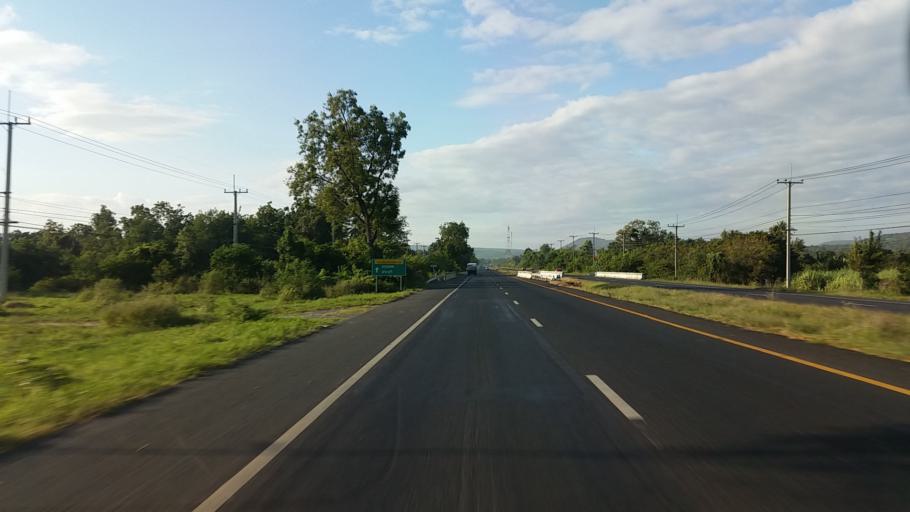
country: TH
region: Lop Buri
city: Phatthana Nikhom
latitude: 15.0087
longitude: 100.9418
